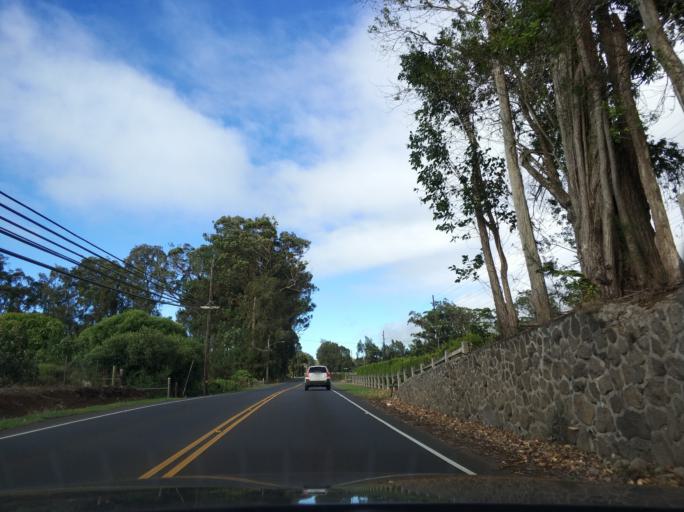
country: US
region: Hawaii
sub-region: Hawaii County
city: Waimea
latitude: 20.0378
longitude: -155.6191
